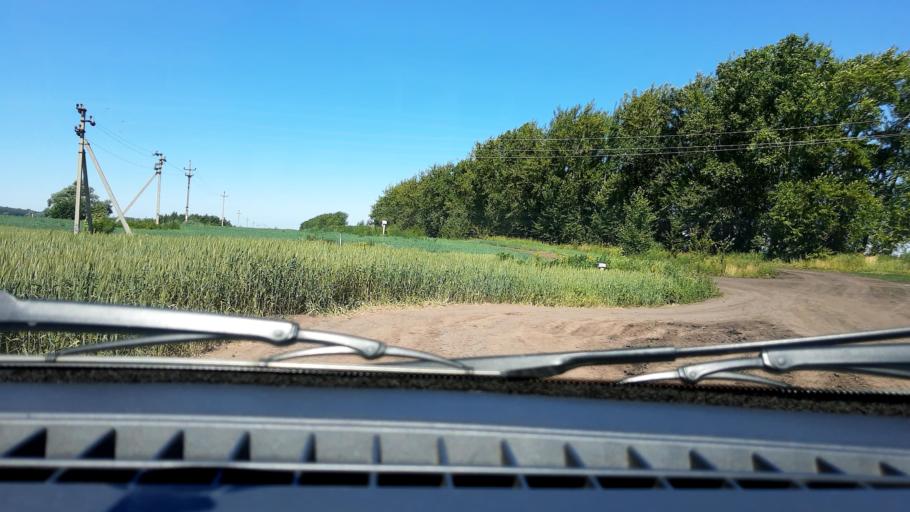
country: RU
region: Bashkortostan
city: Mikhaylovka
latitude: 54.8552
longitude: 55.9466
